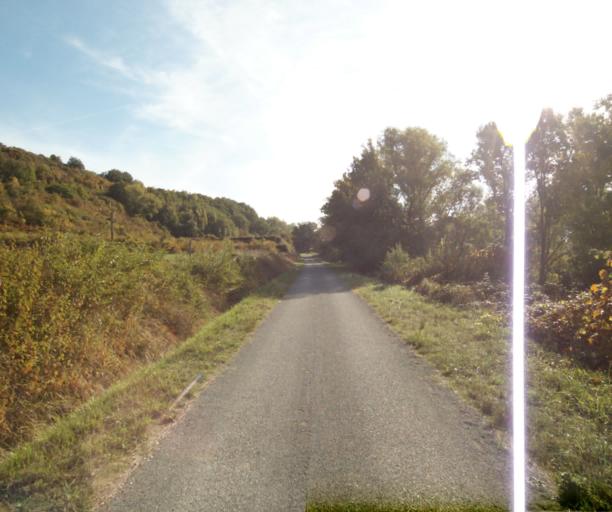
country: FR
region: Midi-Pyrenees
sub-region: Departement du Tarn-et-Garonne
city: Nohic
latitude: 43.9007
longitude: 1.4627
